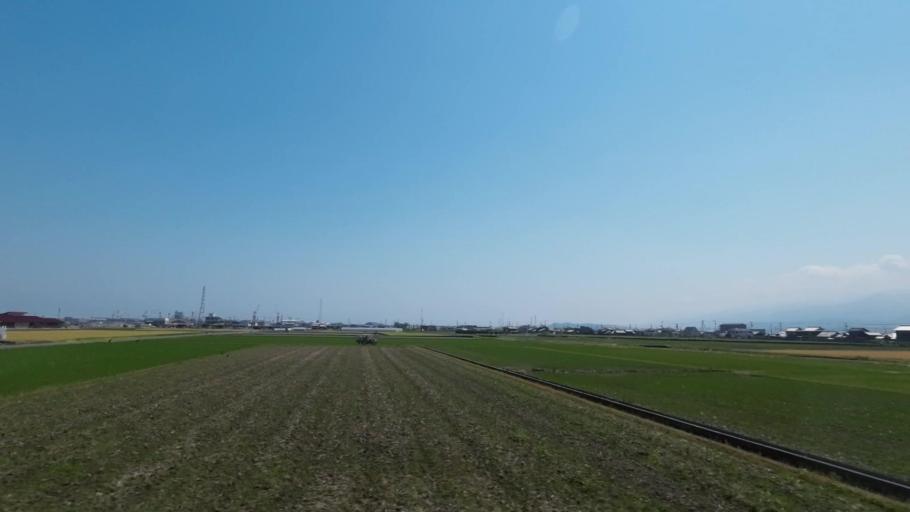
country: JP
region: Ehime
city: Saijo
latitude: 33.9154
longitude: 133.0982
